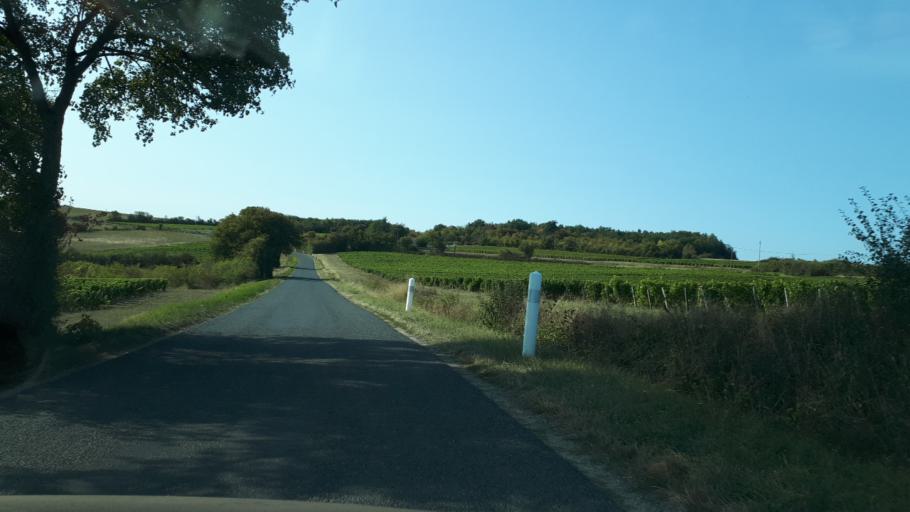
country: FR
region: Centre
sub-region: Departement du Cher
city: Menetou-Salon
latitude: 47.2291
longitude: 2.5185
